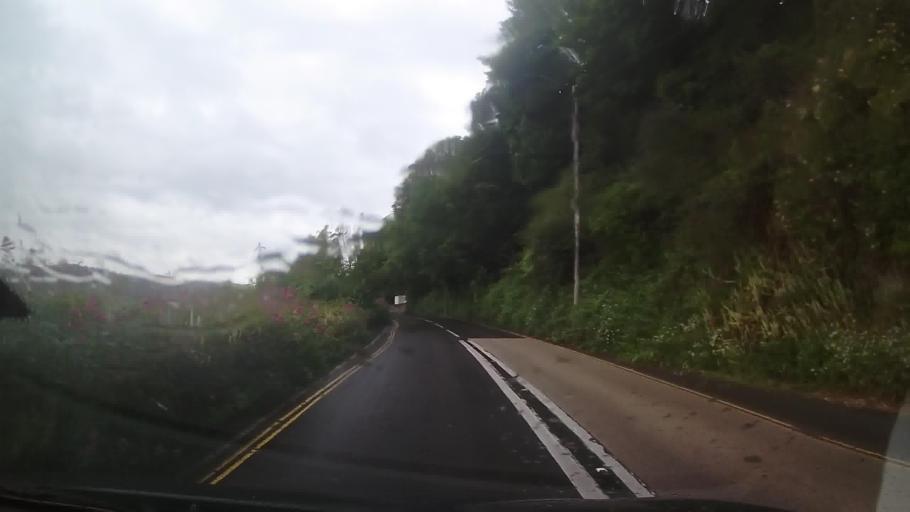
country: GB
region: England
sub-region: Devon
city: Dartmouth
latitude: 50.3603
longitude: -3.5731
